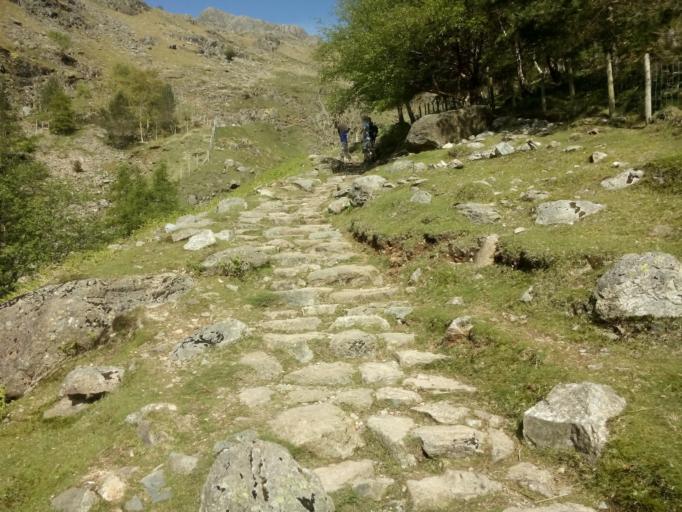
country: GB
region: England
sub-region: Cumbria
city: Ambleside
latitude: 54.4527
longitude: -3.0947
